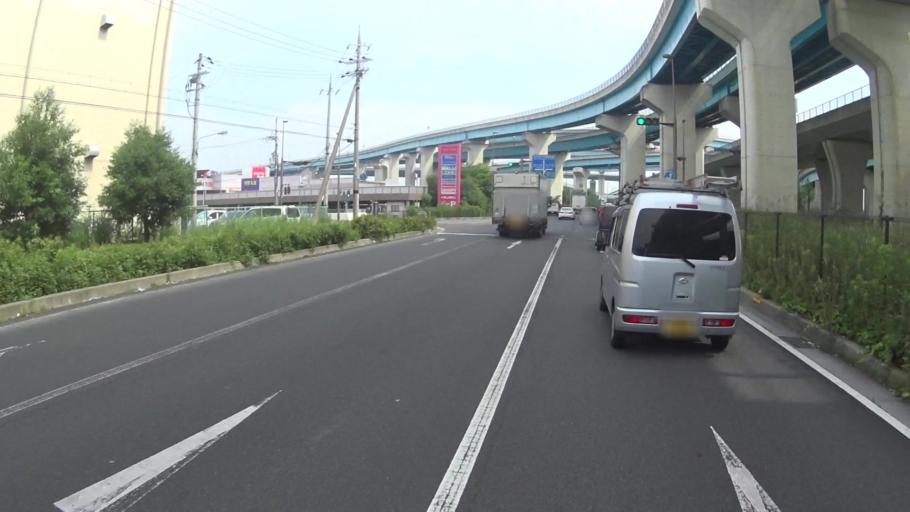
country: JP
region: Kyoto
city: Yawata
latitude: 34.8936
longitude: 135.7489
